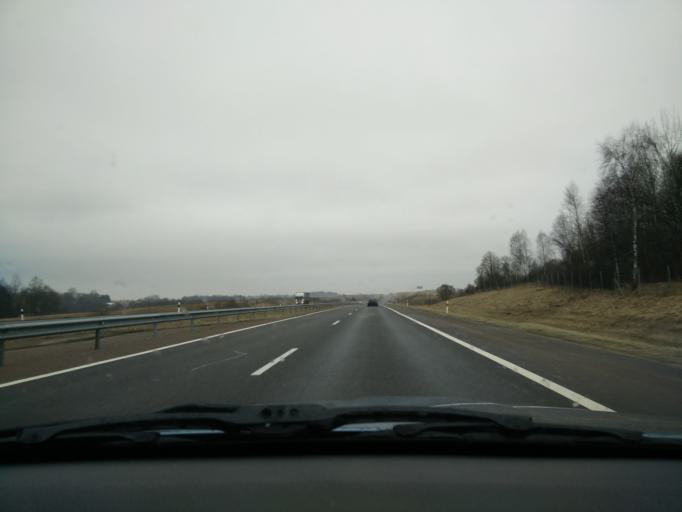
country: LT
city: Silale
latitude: 55.5809
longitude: 22.1540
